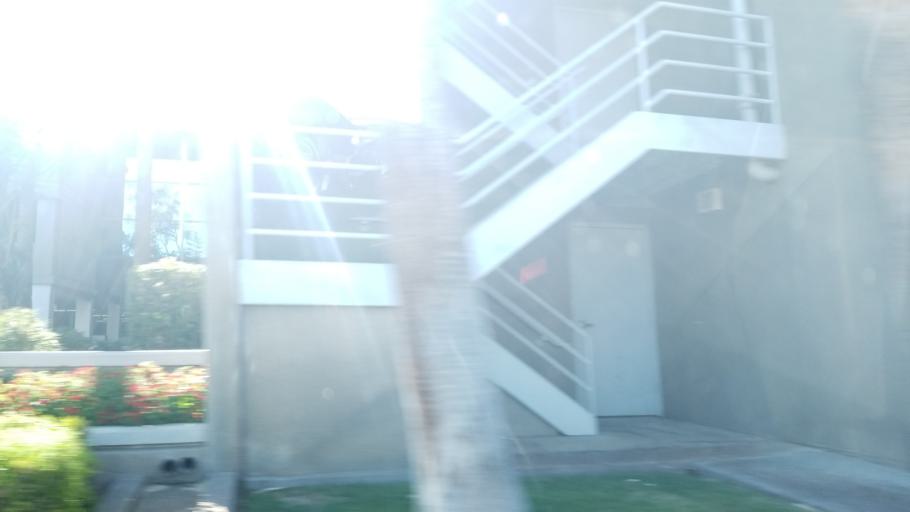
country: US
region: Arizona
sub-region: Maricopa County
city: Phoenix
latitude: 33.4782
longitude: -112.0752
